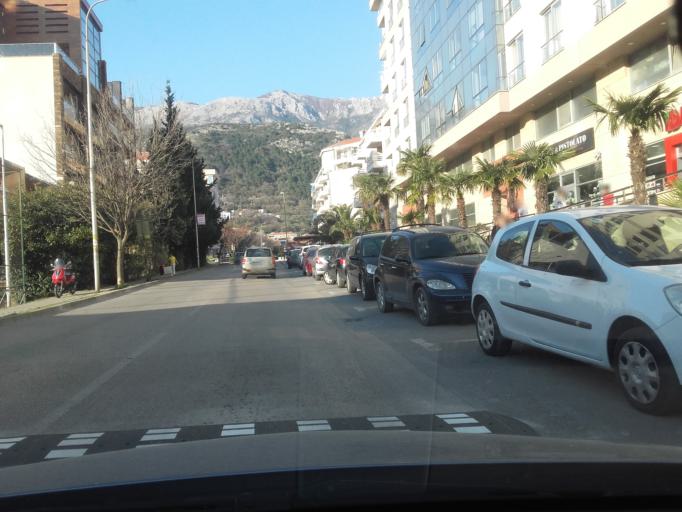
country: ME
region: Budva
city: Budva
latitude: 42.2916
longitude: 18.8377
